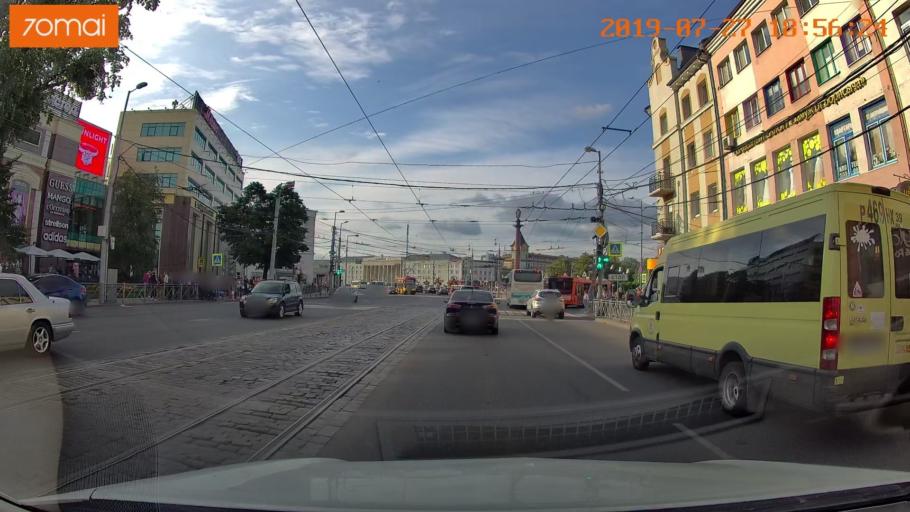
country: RU
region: Kaliningrad
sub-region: Gorod Kaliningrad
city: Kaliningrad
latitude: 54.7183
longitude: 20.5019
